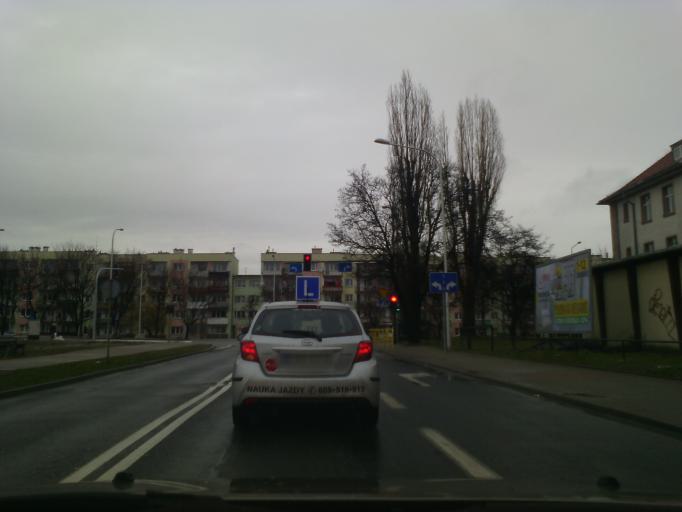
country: PL
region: Lower Silesian Voivodeship
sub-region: Powiat swidnicki
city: Swidnica
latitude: 50.8426
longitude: 16.4649
